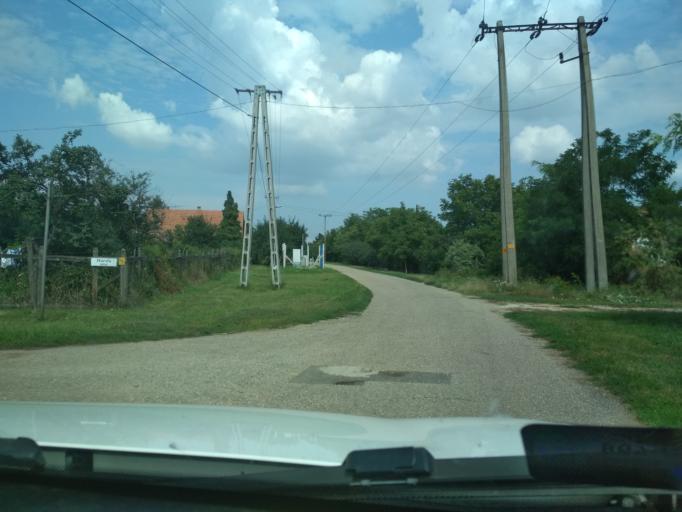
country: HU
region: Jasz-Nagykun-Szolnok
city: Abadszalok
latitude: 47.4679
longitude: 20.6033
